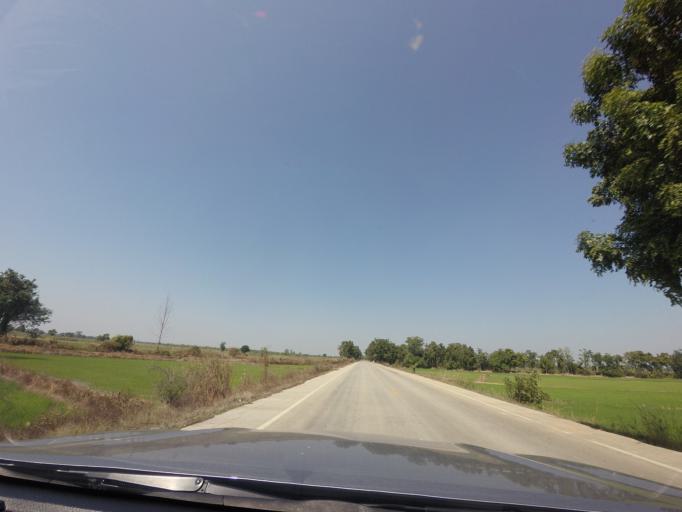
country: TH
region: Sukhothai
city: Ban Na
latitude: 17.0994
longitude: 99.7844
